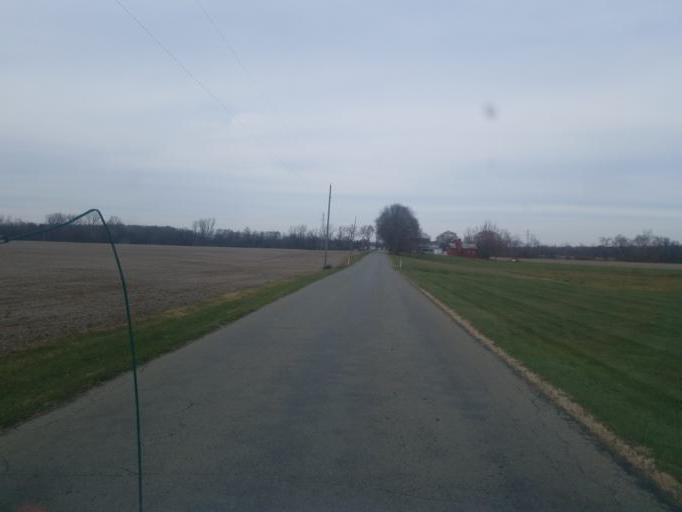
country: US
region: Ohio
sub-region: Knox County
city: Mount Vernon
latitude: 40.4051
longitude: -82.5126
